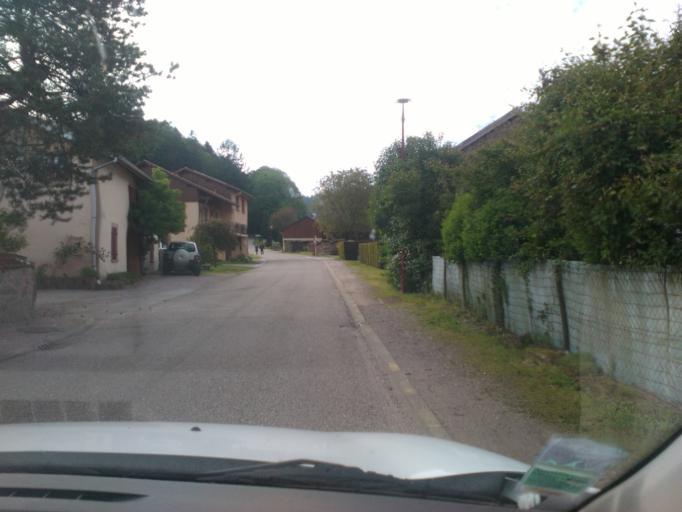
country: FR
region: Lorraine
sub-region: Departement des Vosges
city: Le Tholy
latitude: 48.1187
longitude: 6.7318
